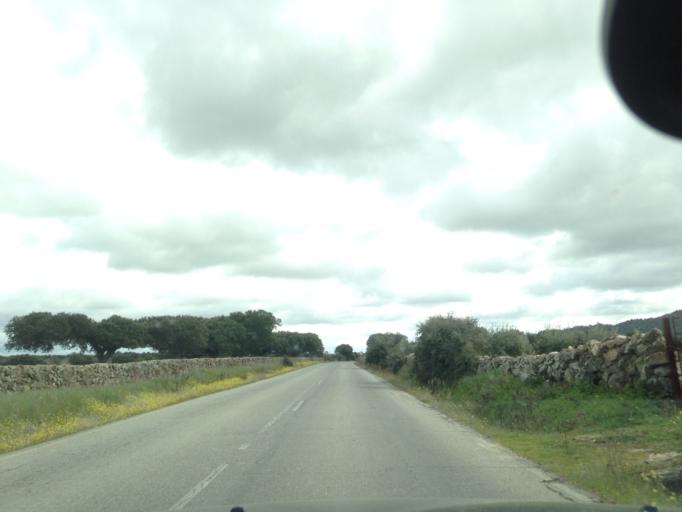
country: ES
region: Extremadura
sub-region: Provincia de Caceres
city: Albala
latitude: 39.2597
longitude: -6.1647
